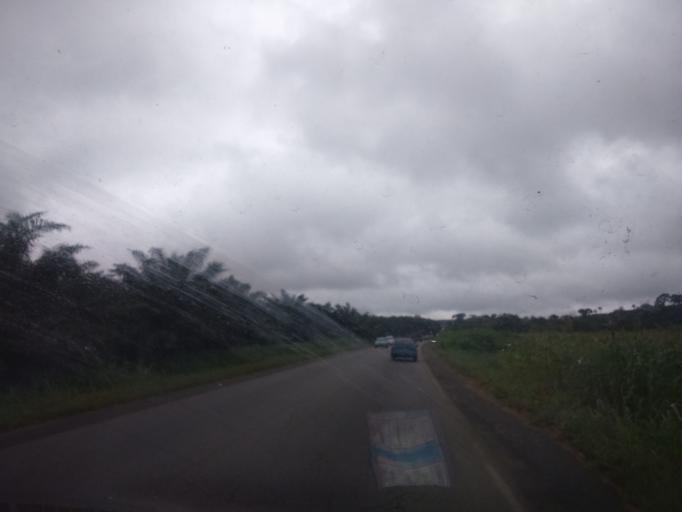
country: CI
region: Sud-Comoe
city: Bonoua
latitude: 5.2804
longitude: -3.5401
